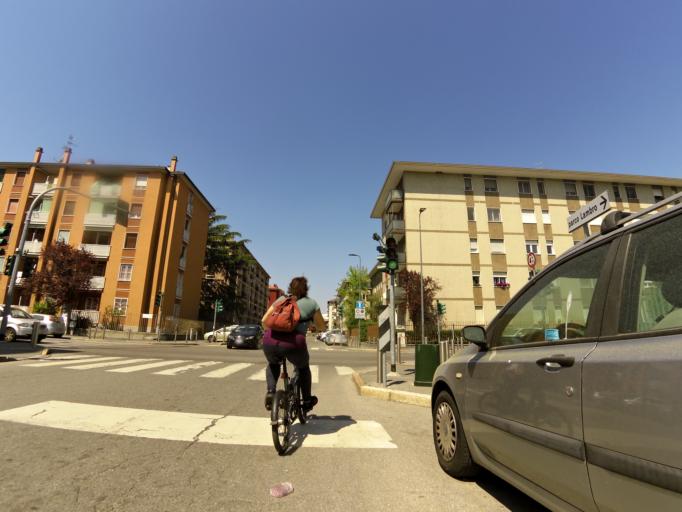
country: IT
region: Lombardy
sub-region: Citta metropolitana di Milano
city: Sesto San Giovanni
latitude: 45.5018
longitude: 9.2469
